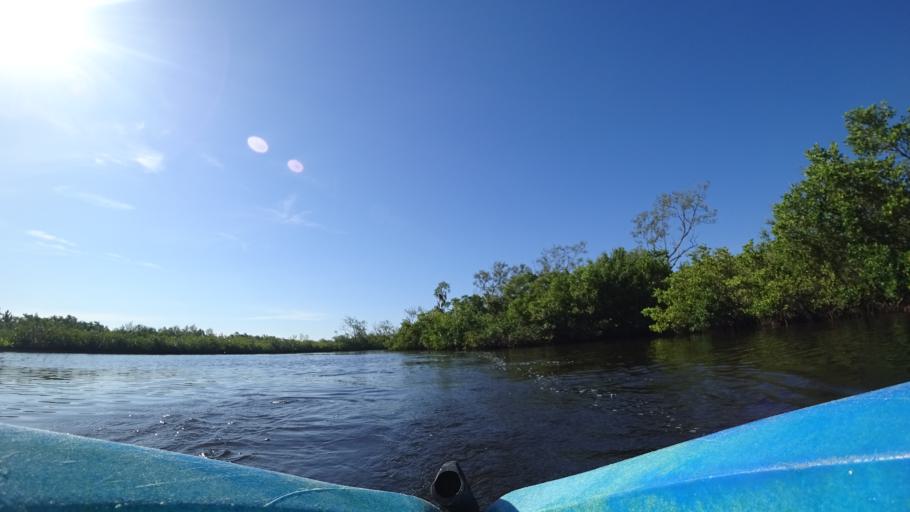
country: US
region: Florida
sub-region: Manatee County
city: Cortez
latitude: 27.5048
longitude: -82.6685
